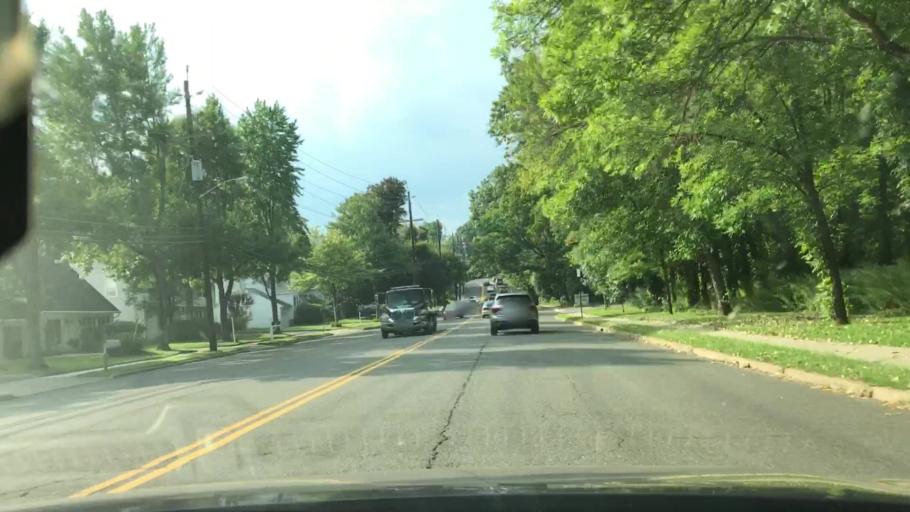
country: US
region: New Jersey
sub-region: Bergen County
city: Rochelle Park
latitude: 40.9176
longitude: -74.0664
